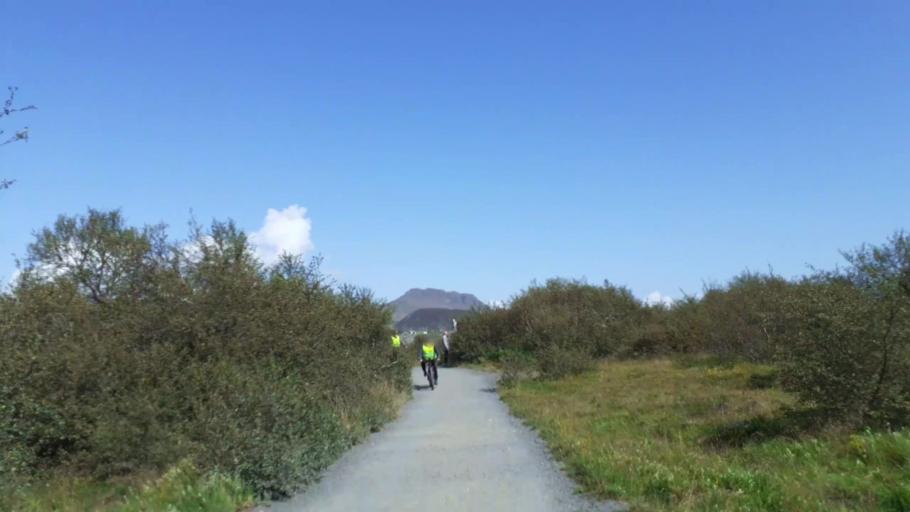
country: IS
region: West
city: Borgarnes
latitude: 64.7552
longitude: -21.5472
